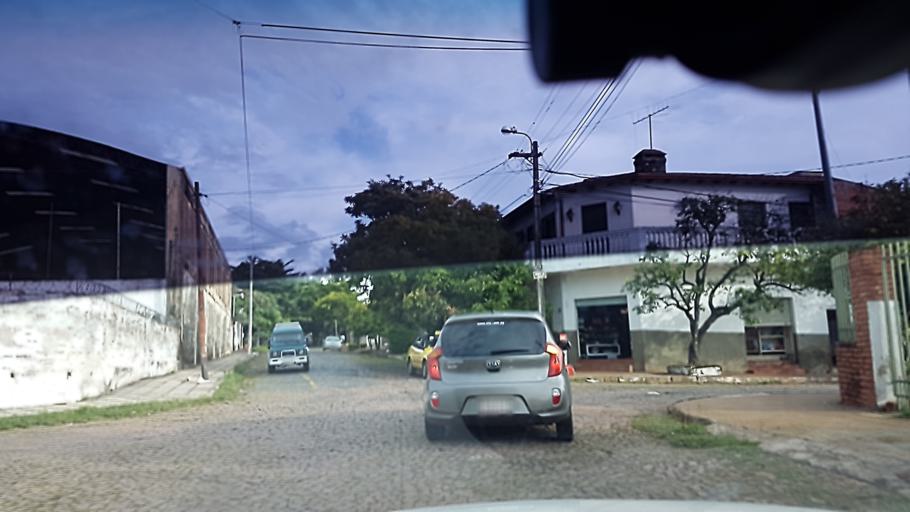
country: PY
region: Central
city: Lambare
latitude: -25.3297
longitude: -57.5785
